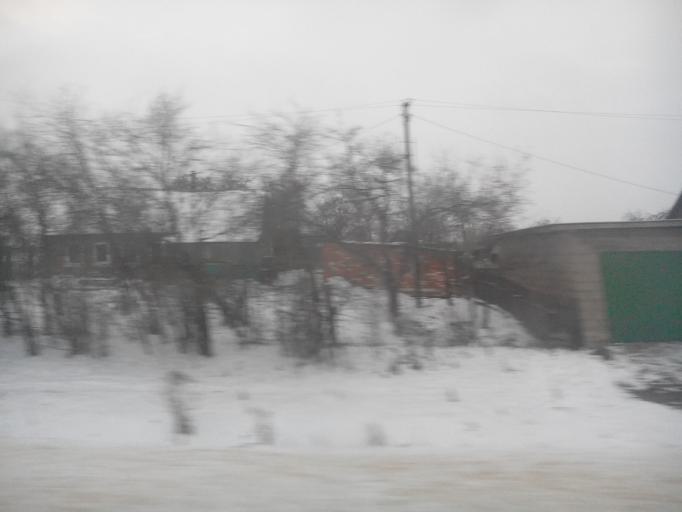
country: RU
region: Tula
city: Plavsk
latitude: 53.7929
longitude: 37.4281
